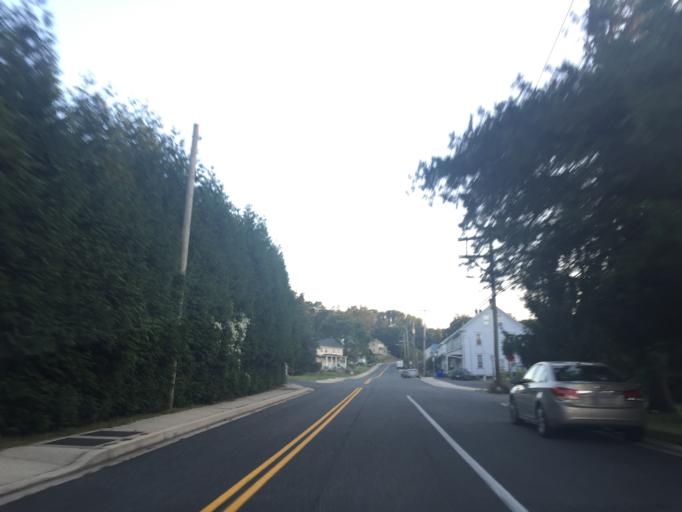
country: US
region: Pennsylvania
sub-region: York County
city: Susquehanna Trails
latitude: 39.7178
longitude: -76.3378
